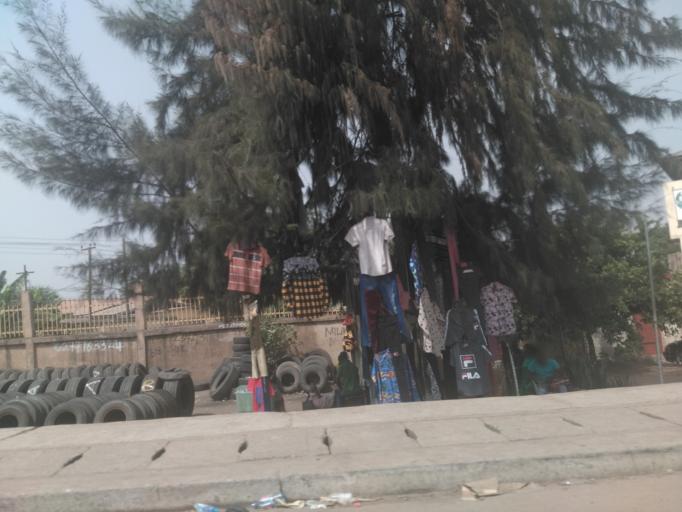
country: GH
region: Greater Accra
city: Dome
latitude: 5.6115
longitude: -0.2312
